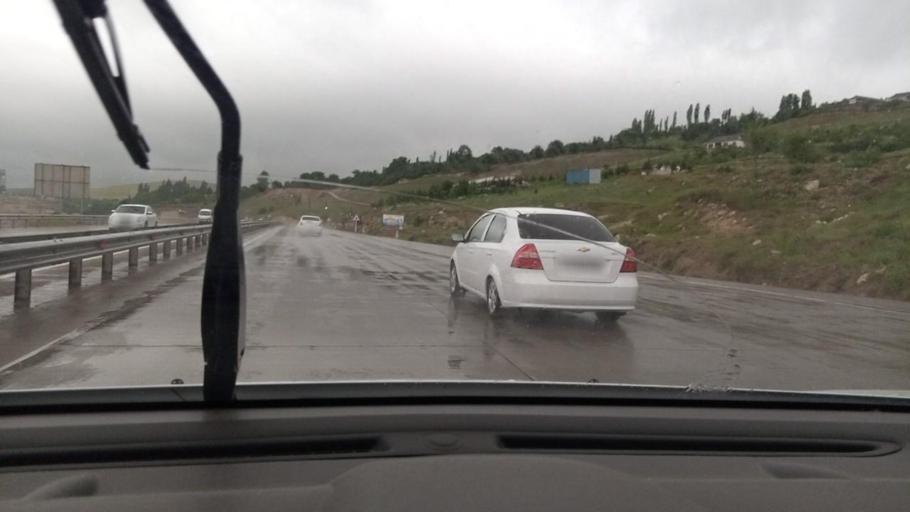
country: UZ
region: Toshkent
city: Angren
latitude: 41.0742
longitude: 70.2670
